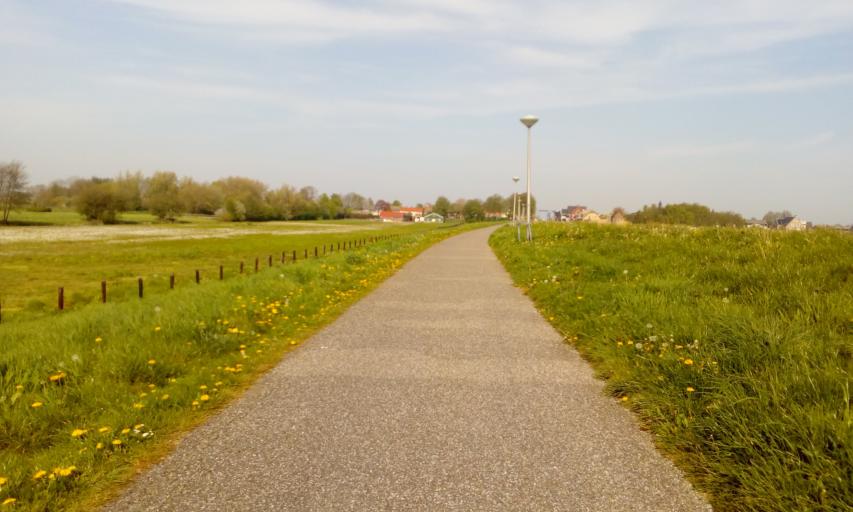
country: NL
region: South Holland
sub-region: Gemeente Kaag en Braassem
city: Leimuiden
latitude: 52.1846
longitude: 4.7034
